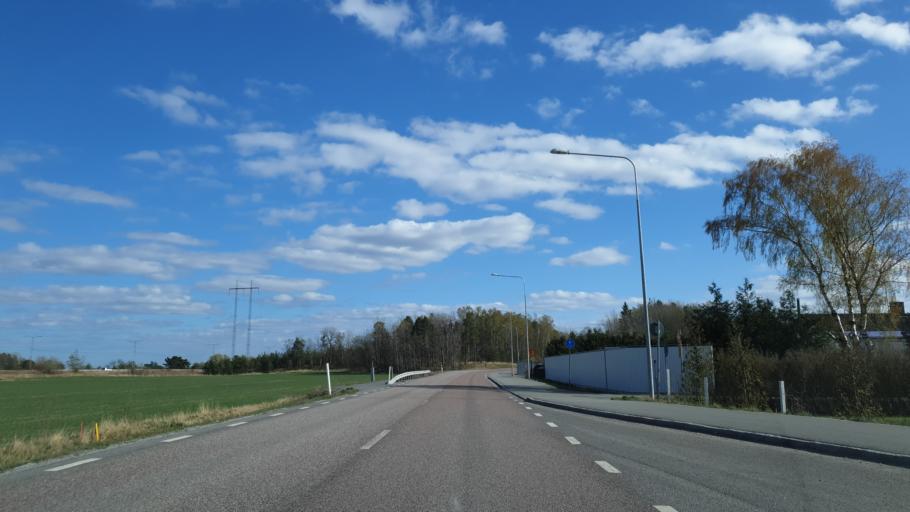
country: SE
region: Stockholm
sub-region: Sigtuna Kommun
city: Rosersberg
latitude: 59.5869
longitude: 17.8954
